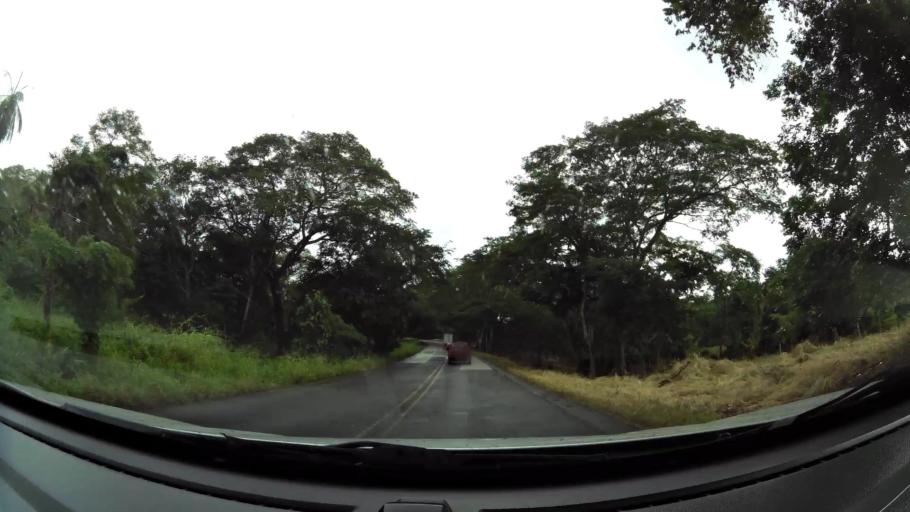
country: CR
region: Guanacaste
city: Juntas
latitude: 10.2221
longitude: -84.9755
